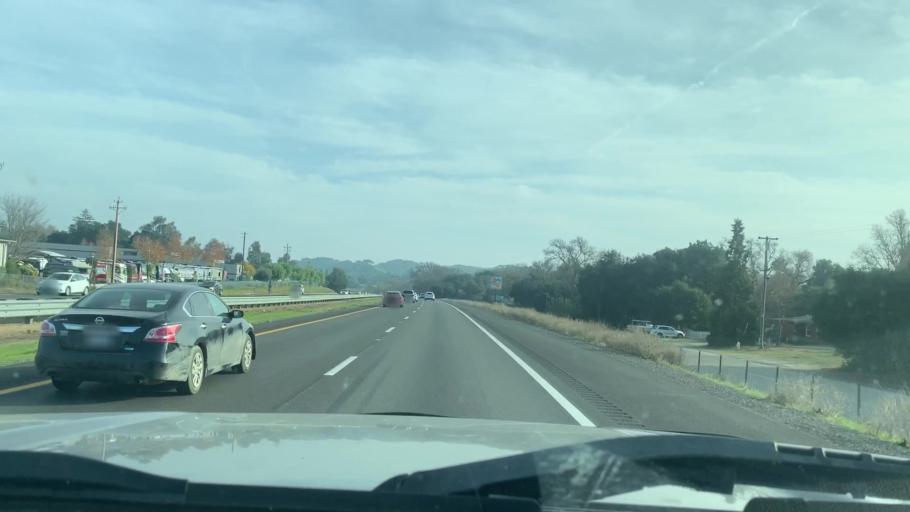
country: US
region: California
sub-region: San Luis Obispo County
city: Atascadero
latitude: 35.5077
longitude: -120.6956
